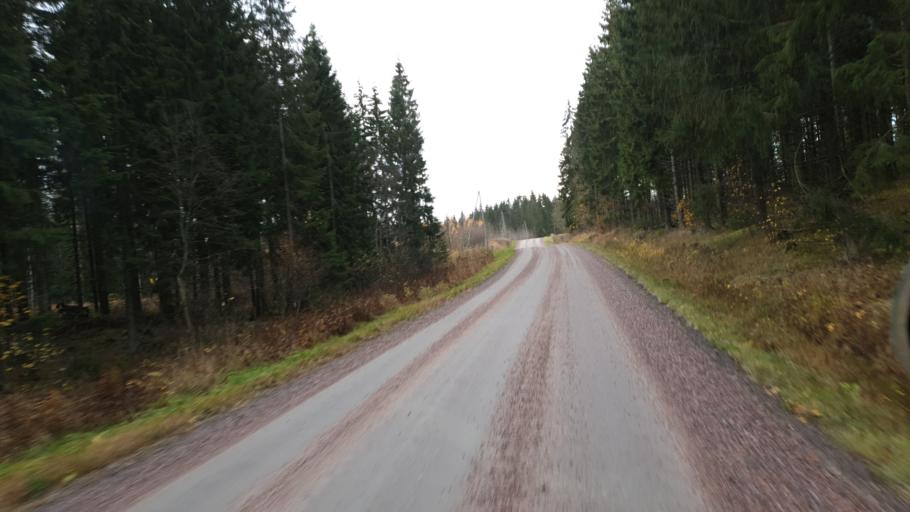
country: FI
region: Uusimaa
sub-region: Helsinki
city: Siuntio
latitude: 60.1512
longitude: 24.2765
